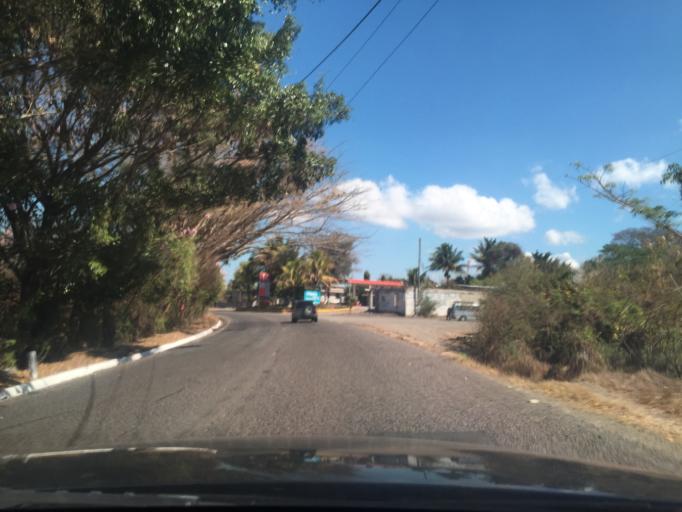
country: GT
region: Chiquimula
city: Ipala
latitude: 14.6133
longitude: -89.6273
